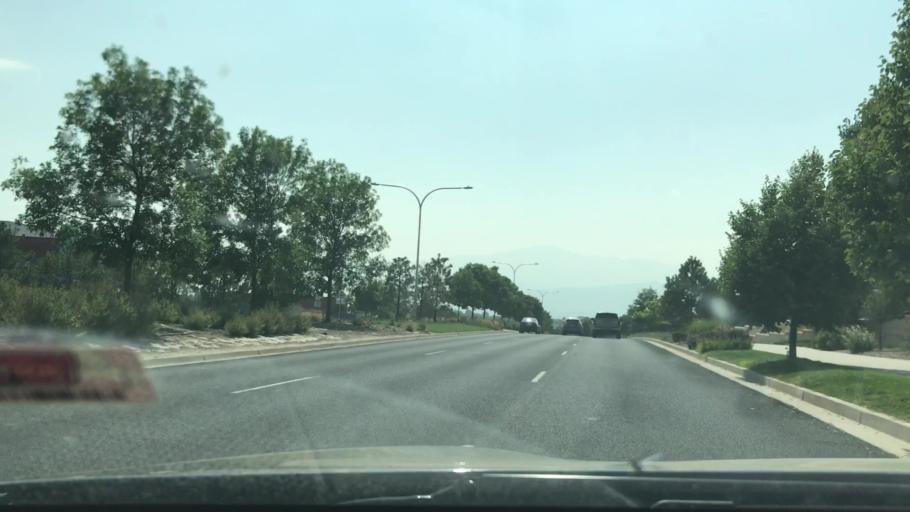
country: US
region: Colorado
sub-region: El Paso County
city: Black Forest
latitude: 38.9699
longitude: -104.7541
